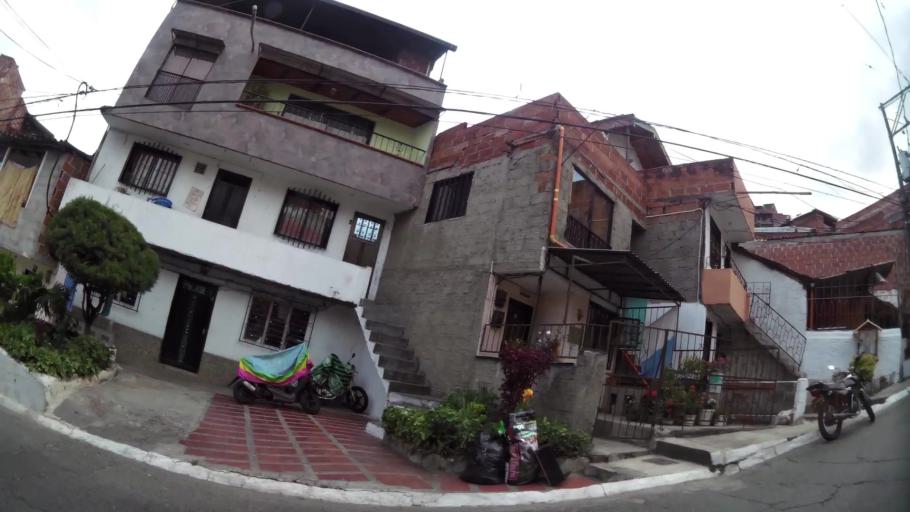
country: CO
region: Antioquia
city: Medellin
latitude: 6.2829
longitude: -75.5487
